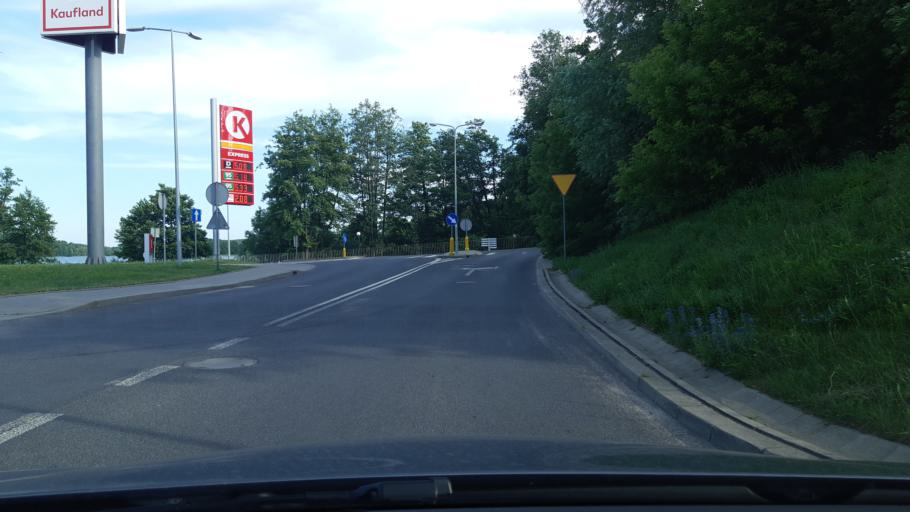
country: PL
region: Warmian-Masurian Voivodeship
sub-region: Powiat mragowski
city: Mragowo
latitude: 53.8778
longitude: 21.3066
